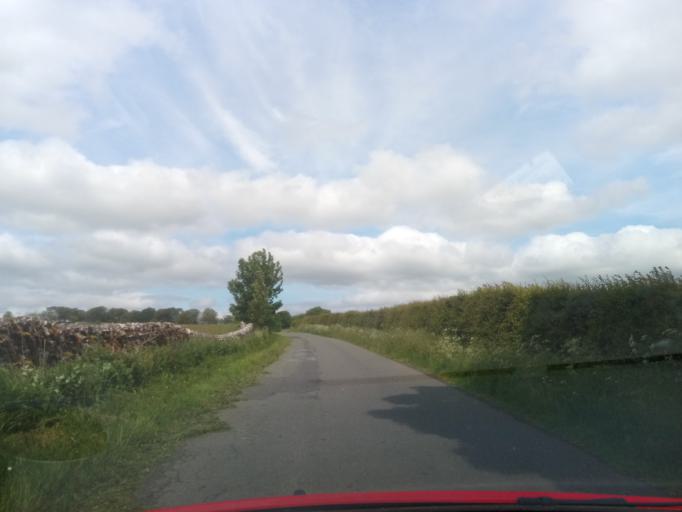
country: GB
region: Scotland
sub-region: The Scottish Borders
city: Selkirk
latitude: 55.5128
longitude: -2.8100
